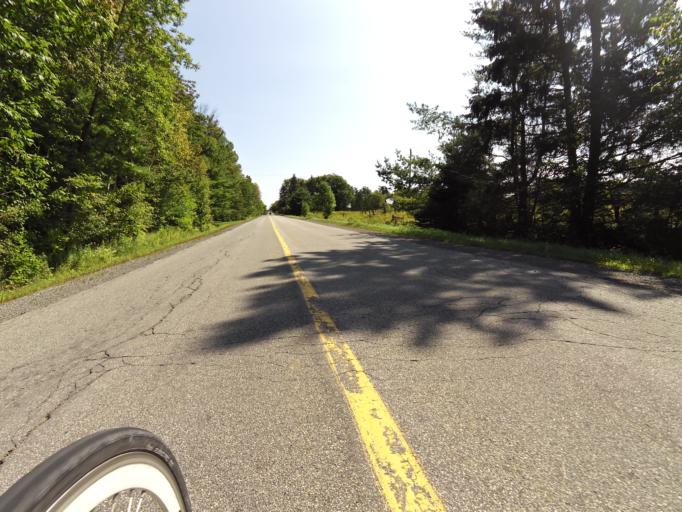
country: CA
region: Ontario
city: Arnprior
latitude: 45.4973
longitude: -76.1464
